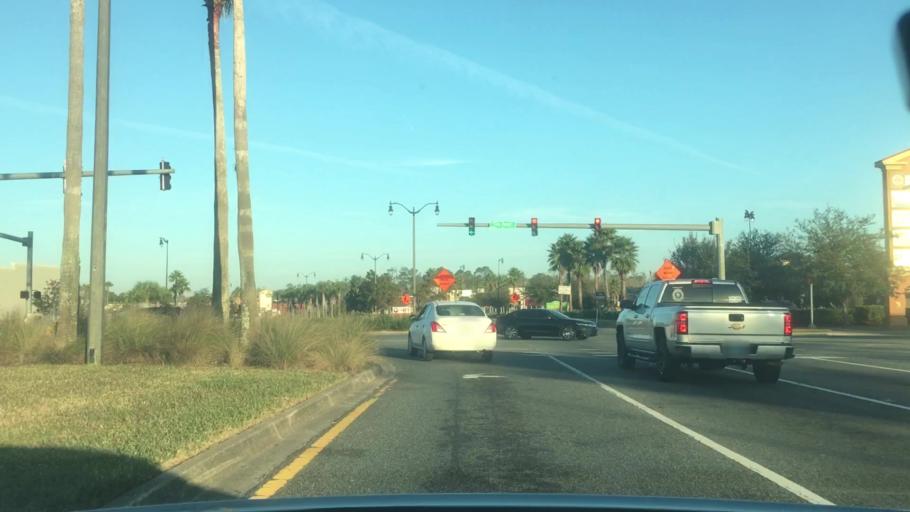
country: US
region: Florida
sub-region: Duval County
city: Jacksonville
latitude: 30.4795
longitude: -81.6359
